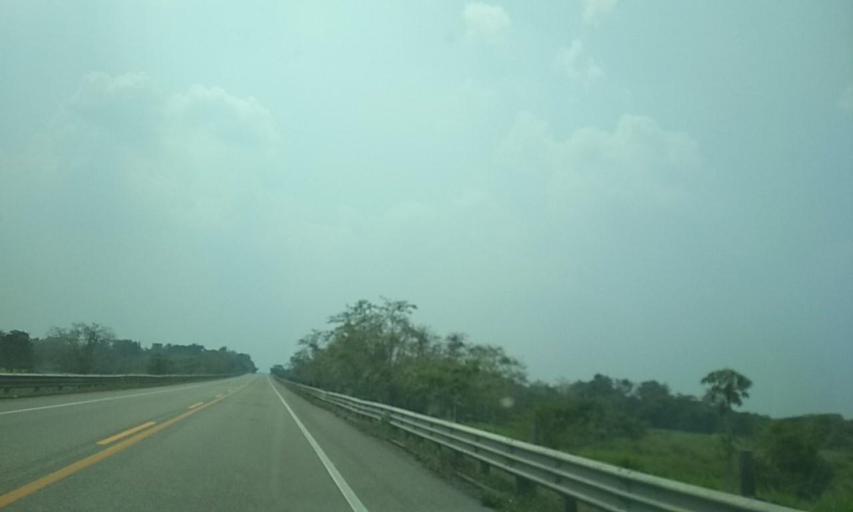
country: MX
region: Tabasco
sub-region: Huimanguillo
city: Francisco Rueda
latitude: 17.7642
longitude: -94.0193
